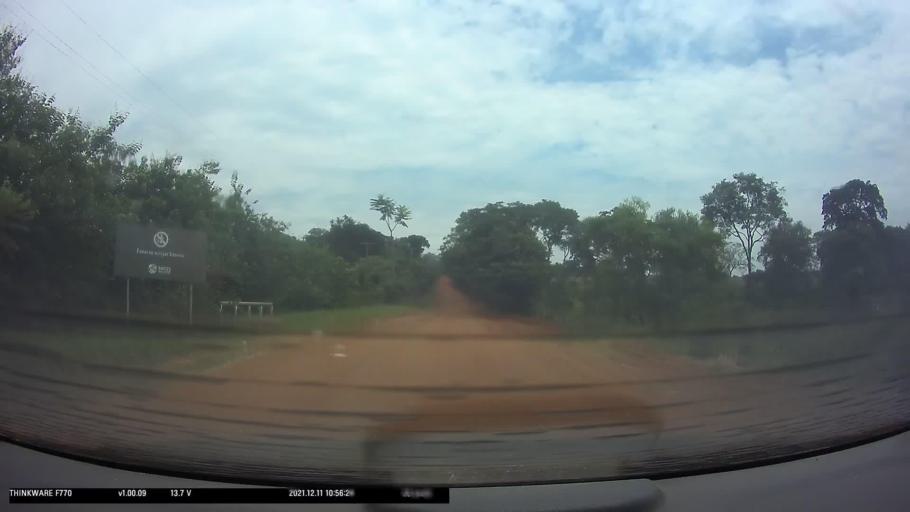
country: PY
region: Cordillera
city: Altos
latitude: -25.2982
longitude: -57.2609
